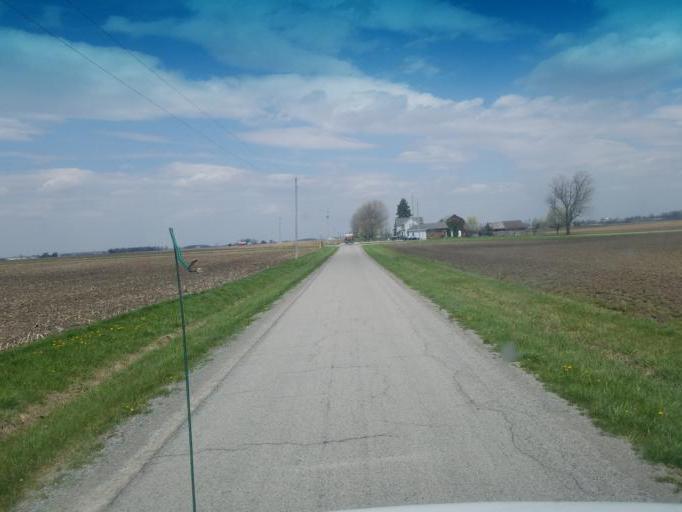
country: US
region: Ohio
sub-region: Wyandot County
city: Upper Sandusky
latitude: 40.8020
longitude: -83.3040
